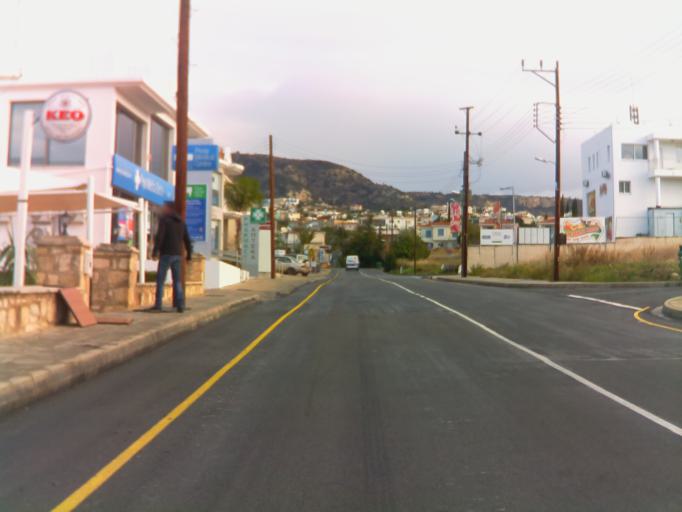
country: CY
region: Pafos
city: Pegeia
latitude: 34.8746
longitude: 32.3791
